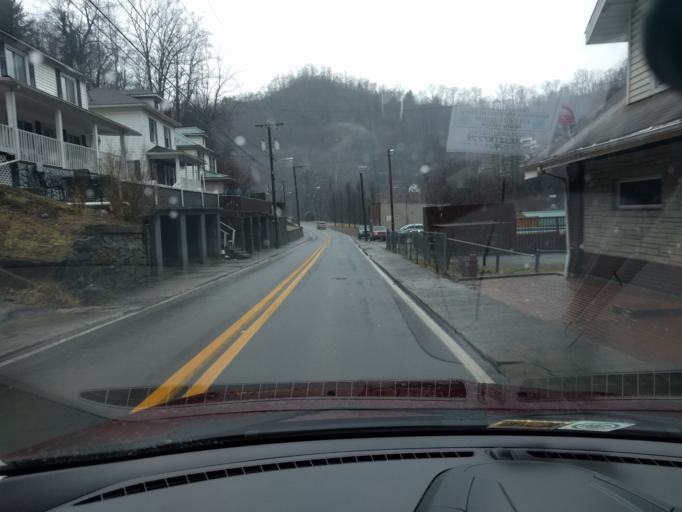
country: US
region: West Virginia
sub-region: McDowell County
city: Welch
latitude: 37.4346
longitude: -81.5765
